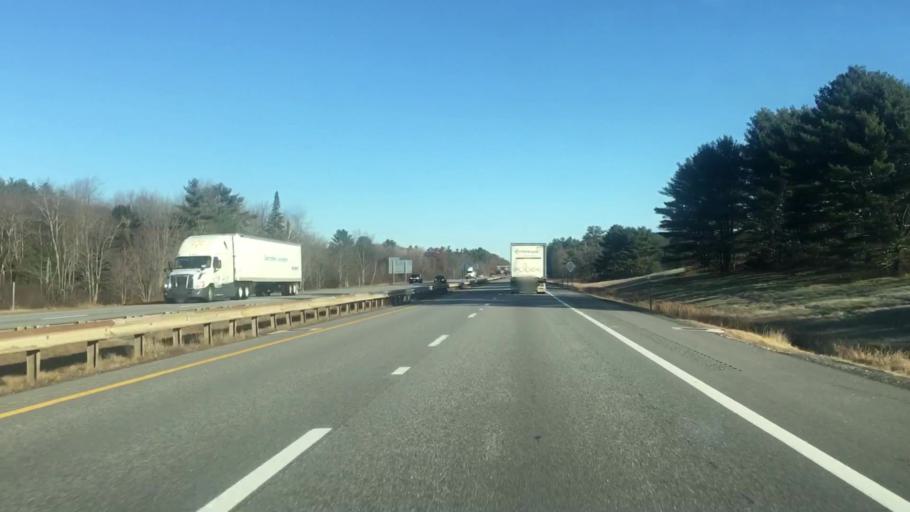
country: US
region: Maine
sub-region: Cumberland County
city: New Gloucester
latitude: 43.9109
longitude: -70.3394
